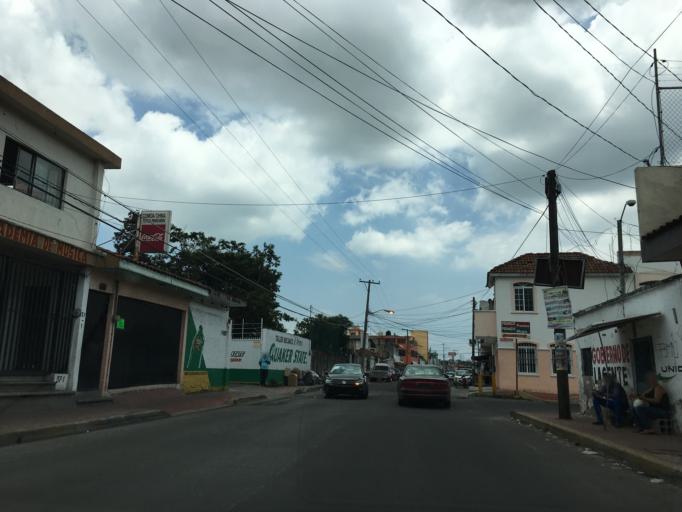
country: MX
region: Nayarit
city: Tepic
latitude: 21.4834
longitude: -104.8884
